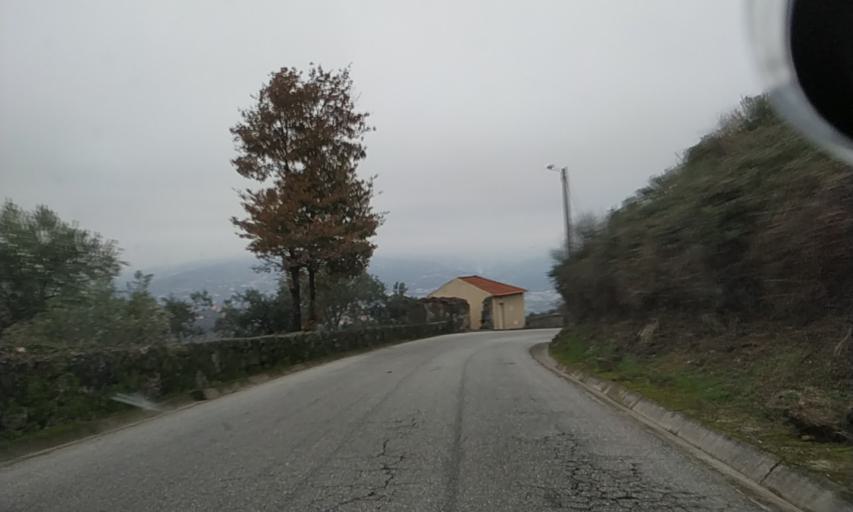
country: PT
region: Viseu
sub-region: Lamego
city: Lamego
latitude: 41.1155
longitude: -7.8035
